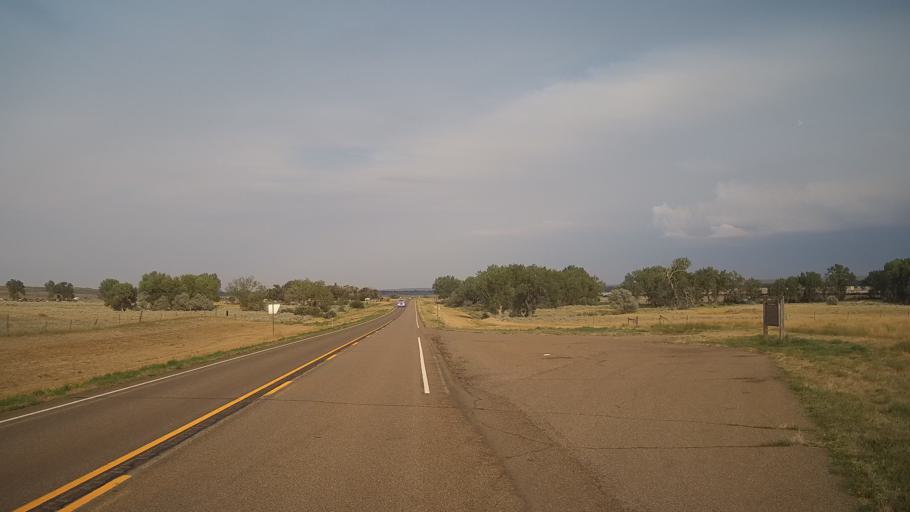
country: US
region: Montana
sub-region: Phillips County
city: Malta
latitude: 48.3692
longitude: -107.9658
